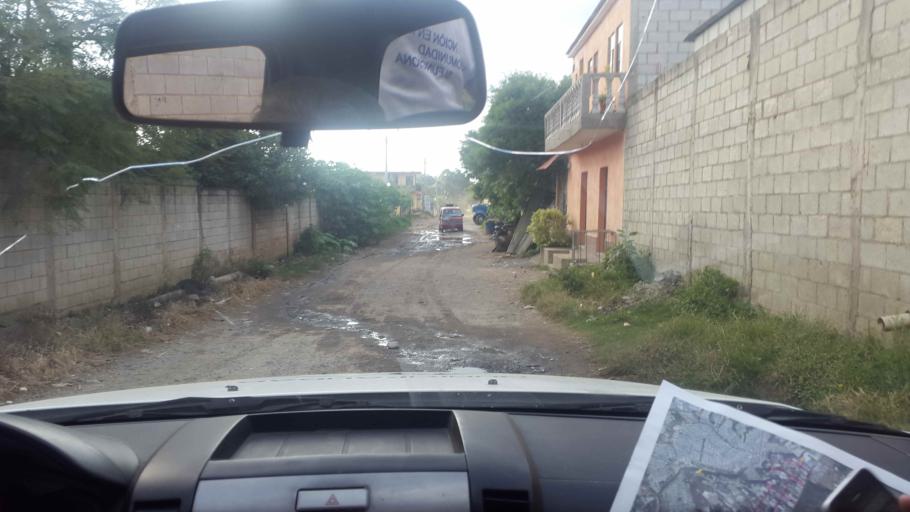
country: GT
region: Guatemala
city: Petapa
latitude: 14.5109
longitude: -90.5403
